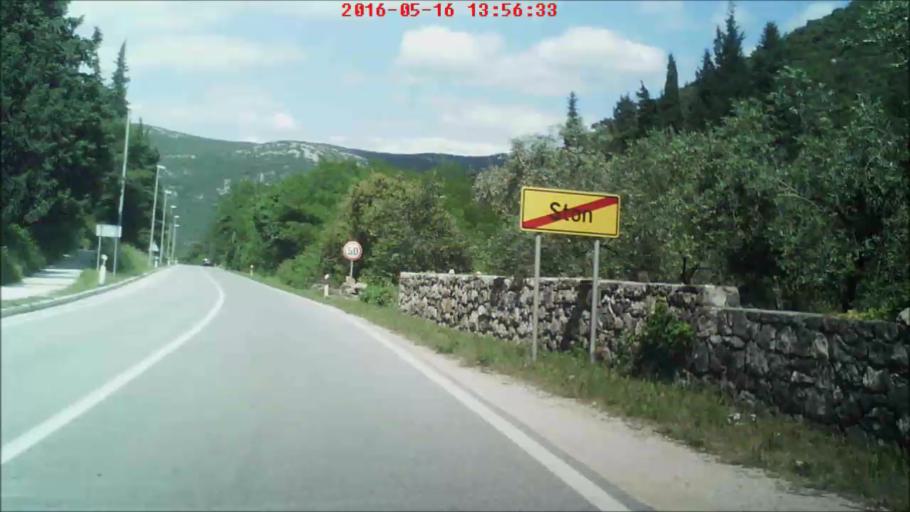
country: HR
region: Dubrovacko-Neretvanska
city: Ston
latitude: 42.8399
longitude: 17.6987
